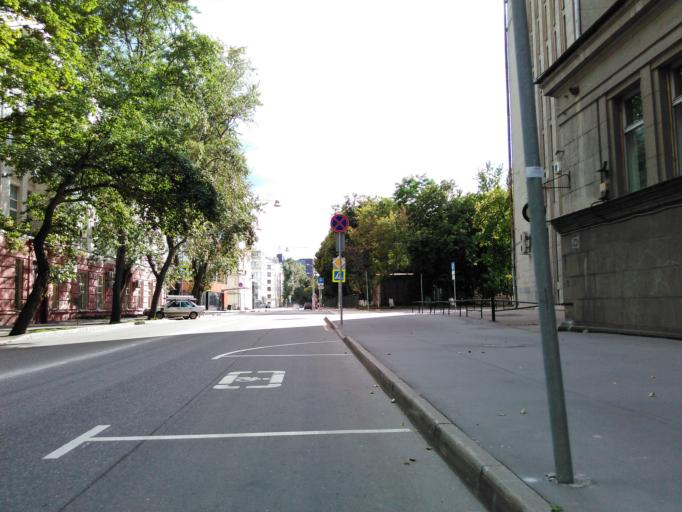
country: RU
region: Moskovskaya
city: Dorogomilovo
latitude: 55.7318
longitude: 37.5743
